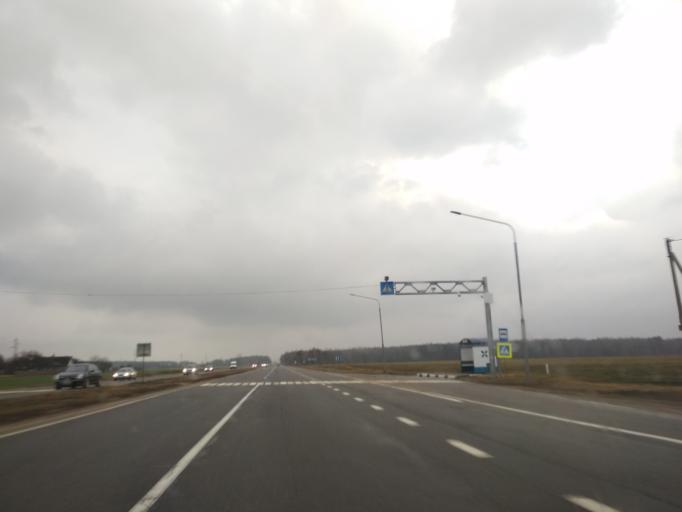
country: BY
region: Minsk
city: Dukora
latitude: 53.6329
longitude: 28.0169
